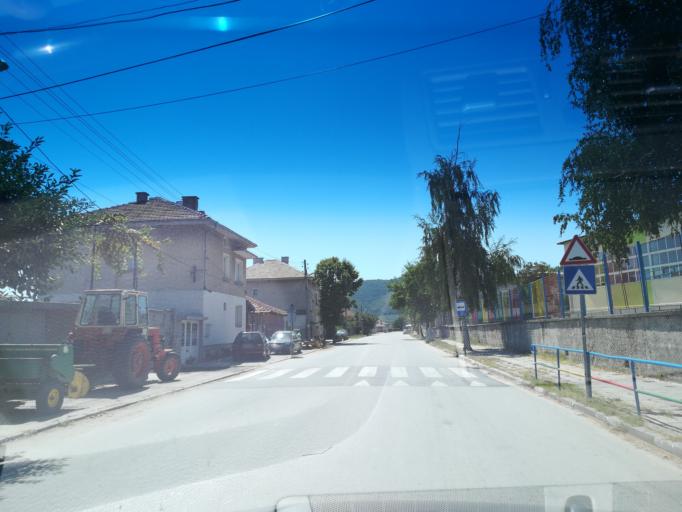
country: BG
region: Pazardzhik
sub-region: Obshtina Strelcha
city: Strelcha
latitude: 42.5028
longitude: 24.3217
